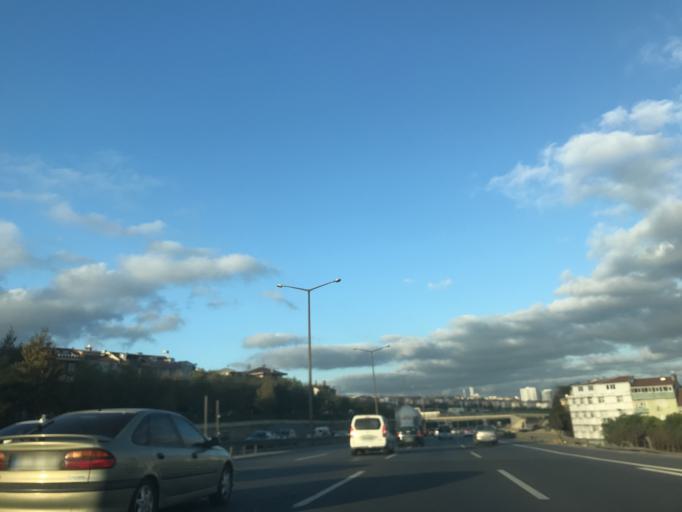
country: TR
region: Istanbul
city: Sultangazi
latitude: 41.0850
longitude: 28.8780
